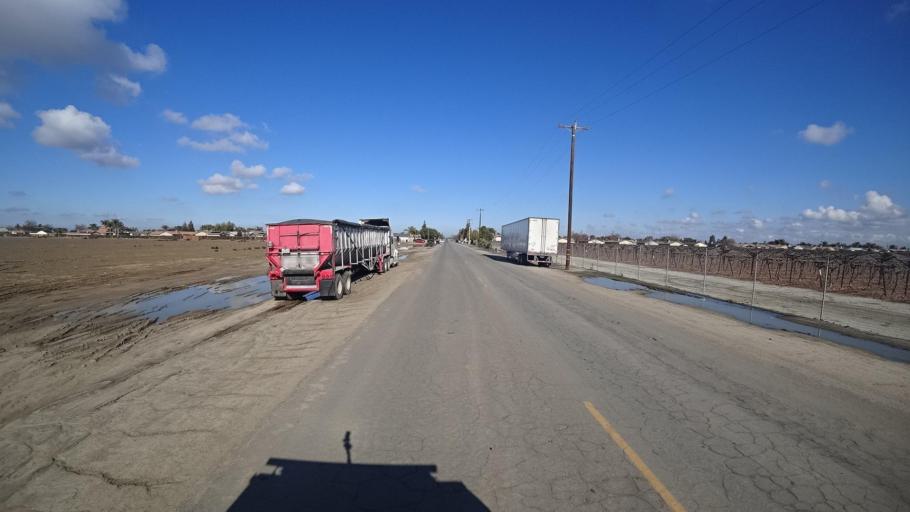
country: US
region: California
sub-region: Kern County
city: McFarland
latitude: 35.6621
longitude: -119.2321
